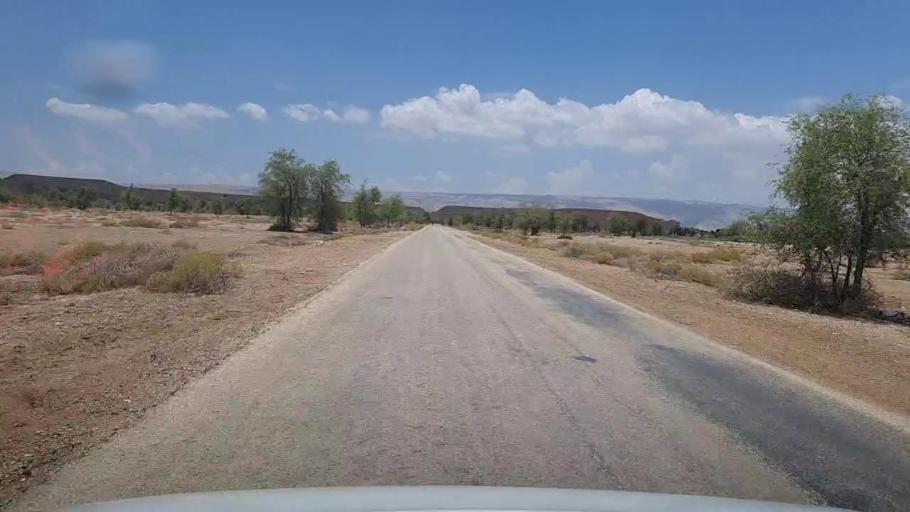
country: PK
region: Sindh
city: Bhan
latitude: 26.3174
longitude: 67.5972
